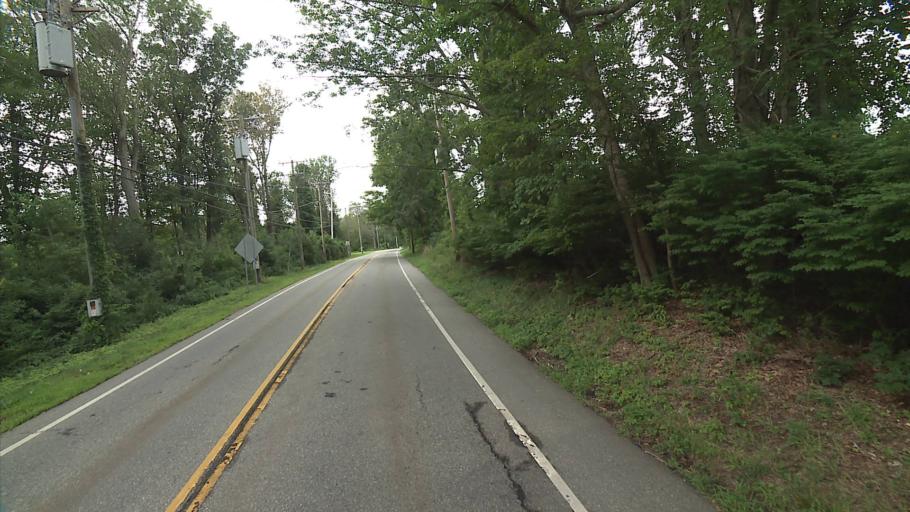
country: US
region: Connecticut
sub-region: New London County
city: Colchester
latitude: 41.5647
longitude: -72.4023
